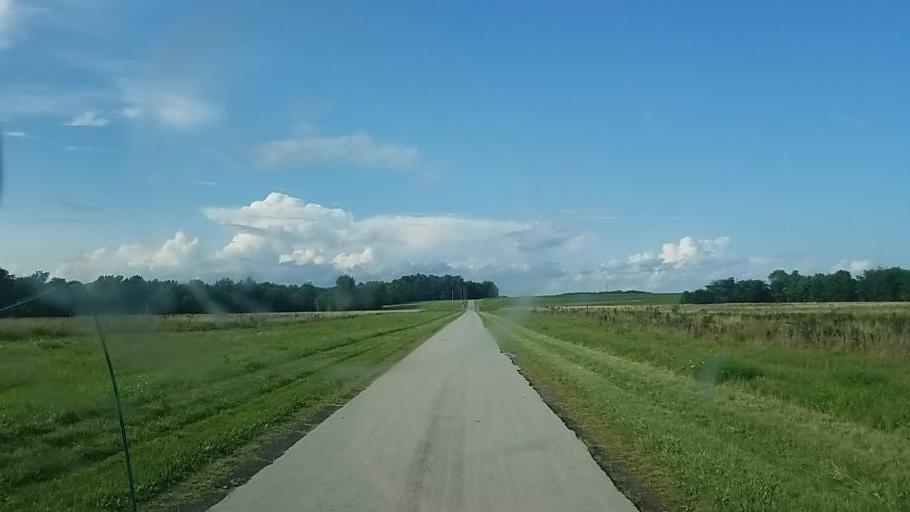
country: US
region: Ohio
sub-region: Wyandot County
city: Upper Sandusky
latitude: 40.7994
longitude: -83.3523
